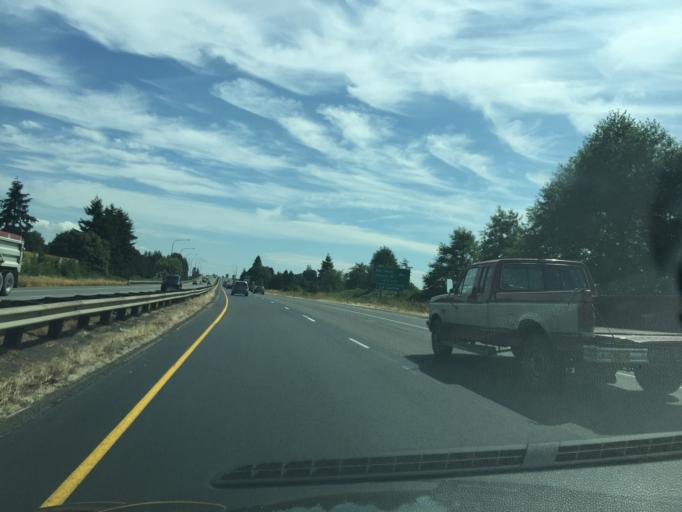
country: US
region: Washington
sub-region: Skagit County
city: Burlington
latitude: 48.4781
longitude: -122.3426
